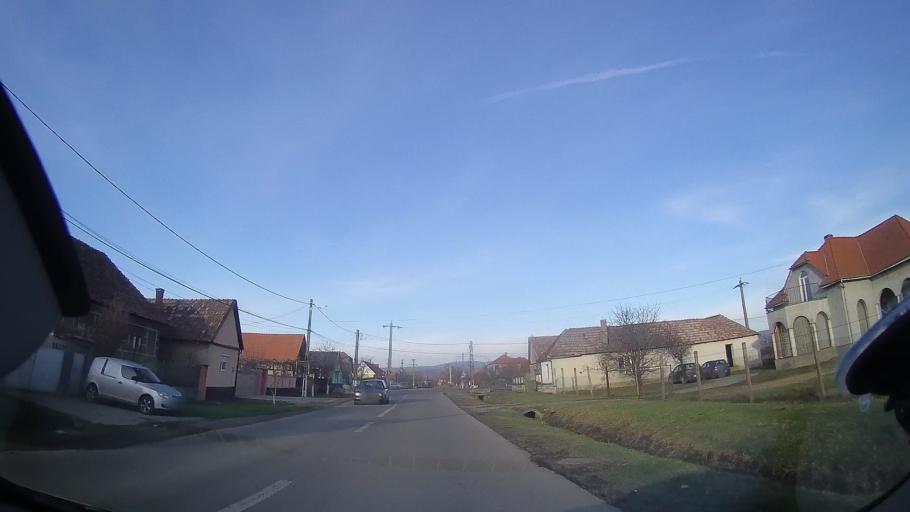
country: RO
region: Bihor
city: Lugasu de Jos
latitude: 47.0423
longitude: 22.3534
